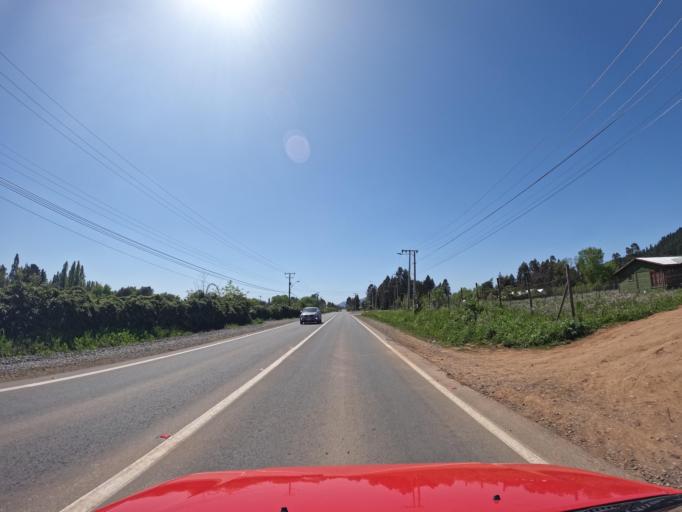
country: CL
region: Maule
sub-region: Provincia de Linares
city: Colbun
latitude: -35.7251
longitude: -71.4179
